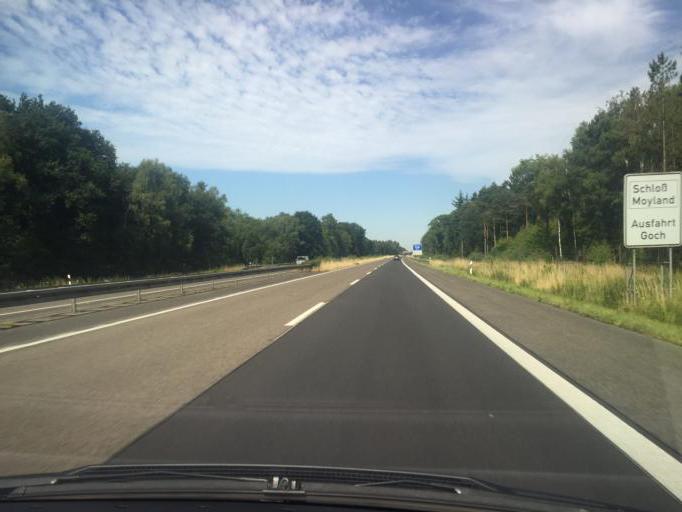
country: DE
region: North Rhine-Westphalia
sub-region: Regierungsbezirk Dusseldorf
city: Weeze
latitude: 51.6497
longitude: 6.2217
